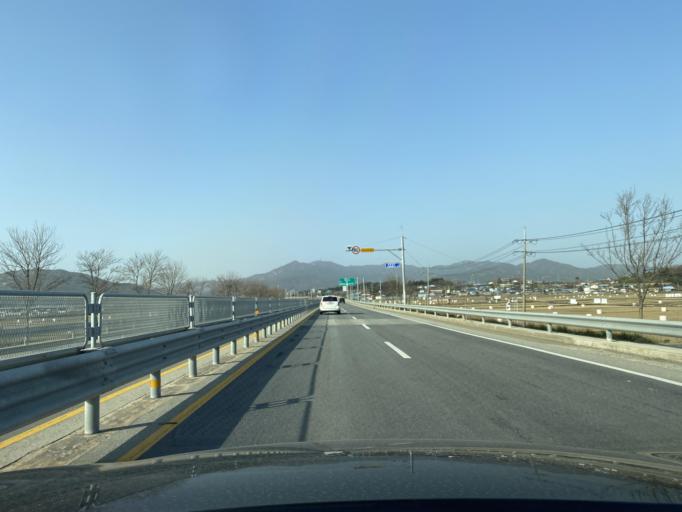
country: KR
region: Chungcheongnam-do
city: Hongsung
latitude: 36.6899
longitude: 126.7063
